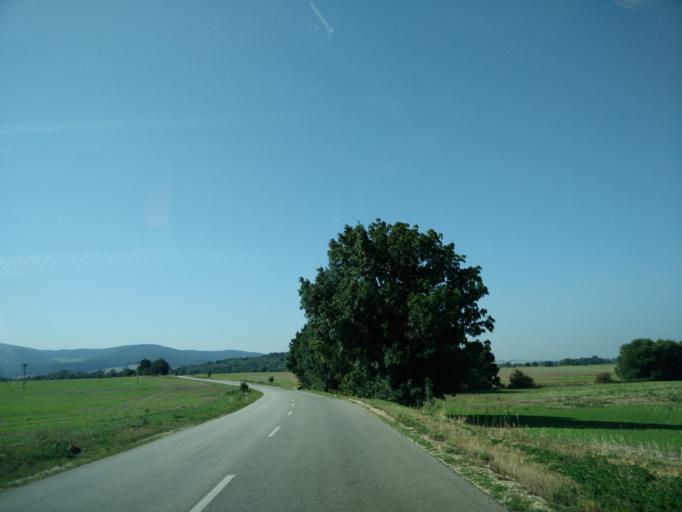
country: SK
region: Nitriansky
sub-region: Okres Nitra
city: Nitra
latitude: 48.3981
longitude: 18.1139
